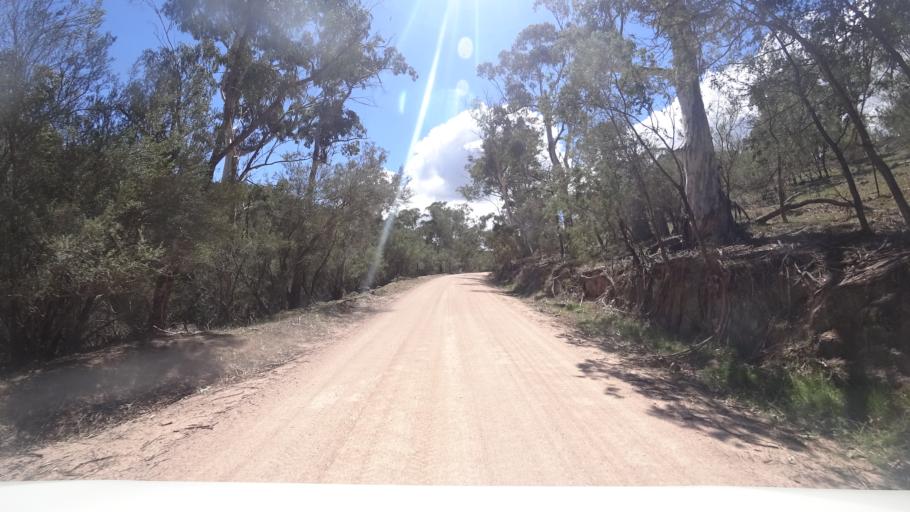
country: AU
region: New South Wales
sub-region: Oberon
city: Oberon
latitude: -33.5442
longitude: 149.9321
